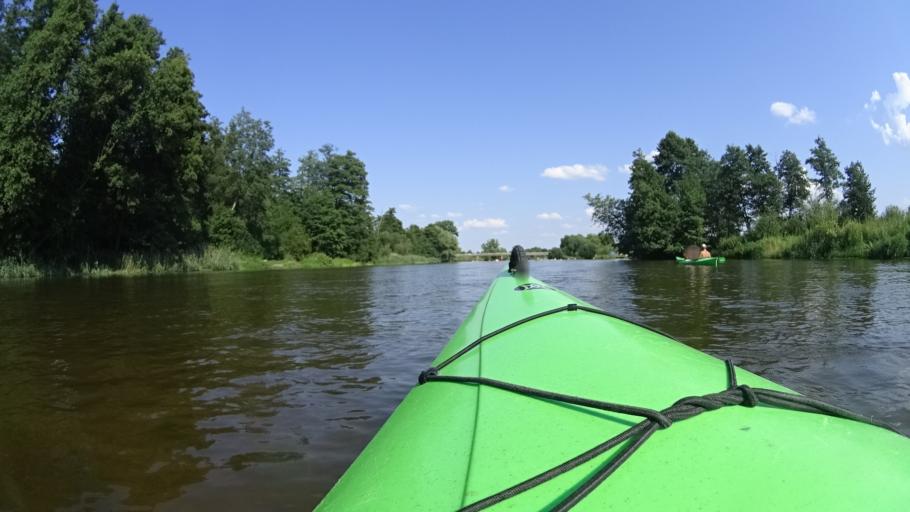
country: PL
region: Masovian Voivodeship
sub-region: Powiat bialobrzeski
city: Bialobrzegi
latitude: 51.6654
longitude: 20.9140
